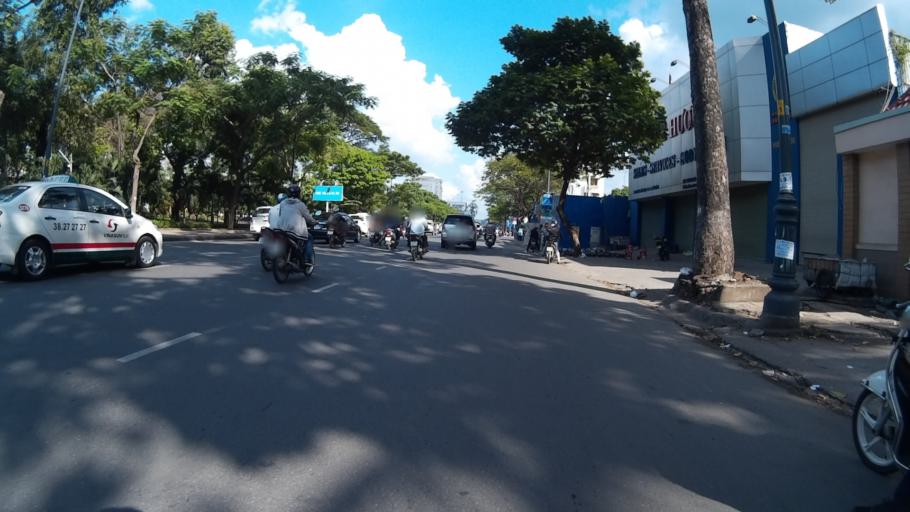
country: VN
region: Ho Chi Minh City
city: Quan Phu Nhuan
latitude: 10.8003
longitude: 106.6647
